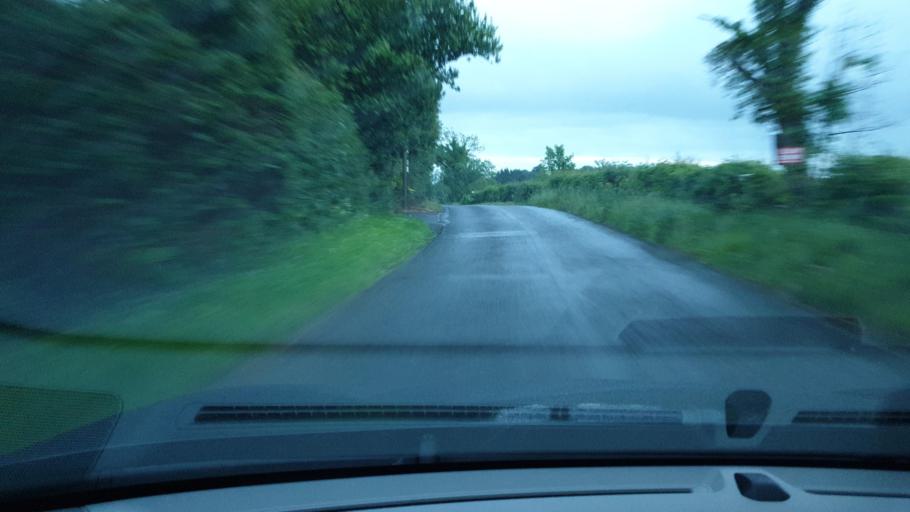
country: IE
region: Leinster
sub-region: An Mhi
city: Ashbourne
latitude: 53.5297
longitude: -6.3396
